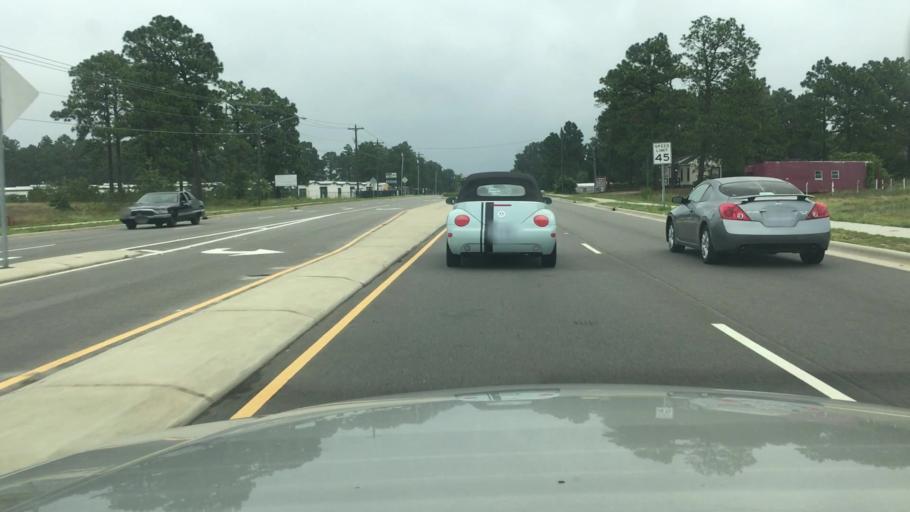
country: US
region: North Carolina
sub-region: Cumberland County
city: Hope Mills
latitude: 35.0090
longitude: -78.9116
